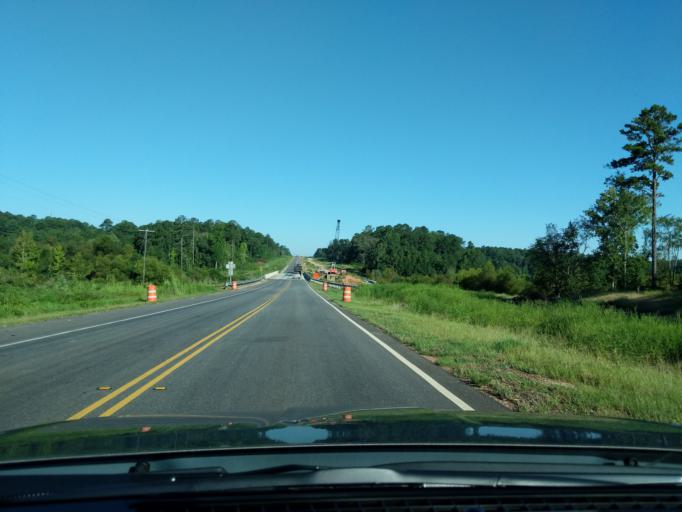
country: US
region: Georgia
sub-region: McDuffie County
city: Thomson
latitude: 33.5805
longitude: -82.5291
